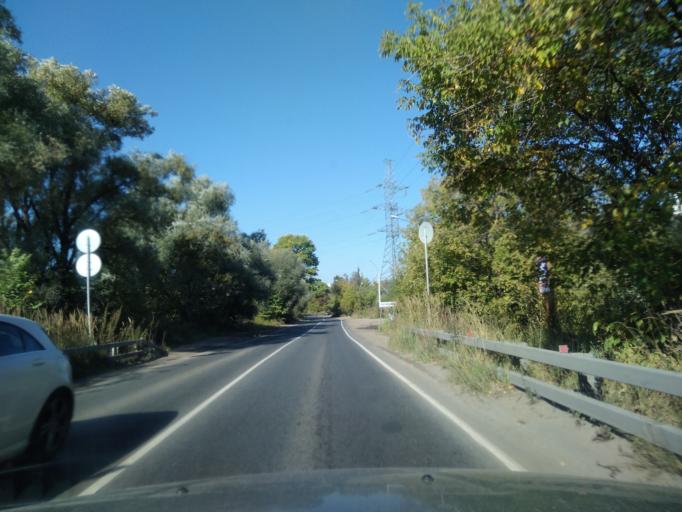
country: RU
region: Moscow
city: Strogino
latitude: 55.8545
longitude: 37.3907
